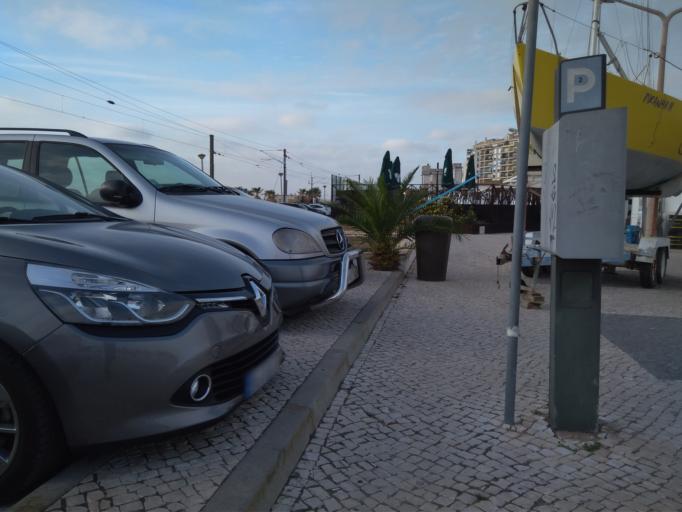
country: PT
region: Faro
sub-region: Faro
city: Faro
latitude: 37.0156
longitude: -7.9374
